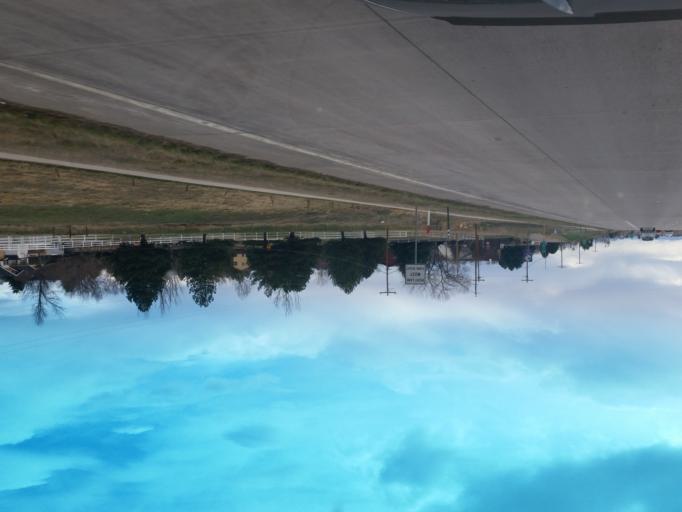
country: US
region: Colorado
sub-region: Weld County
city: Greeley
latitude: 40.3922
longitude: -104.7765
